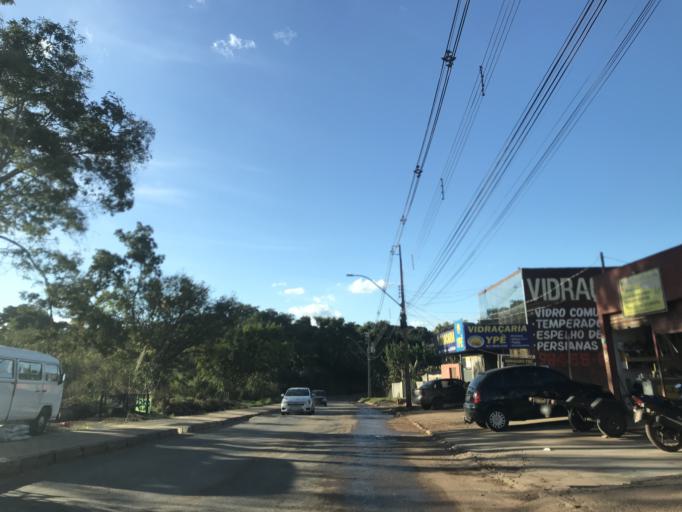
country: BR
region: Federal District
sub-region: Brasilia
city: Brasilia
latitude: -15.8828
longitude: -47.7804
